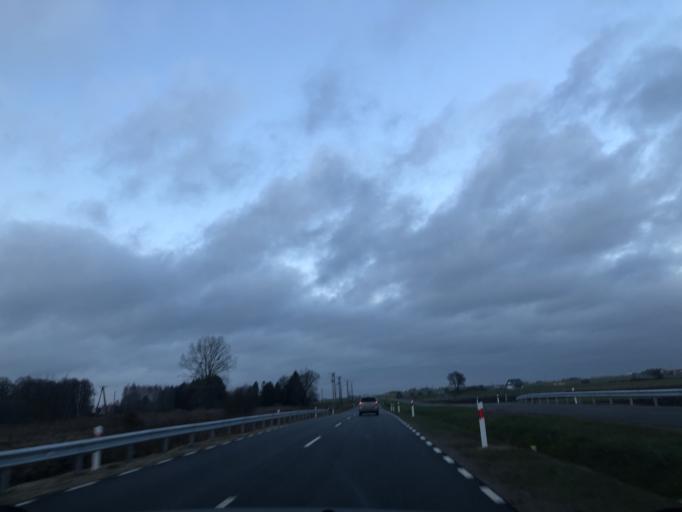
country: PL
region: Podlasie
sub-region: Lomza
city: Lomza
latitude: 53.1336
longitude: 22.0496
